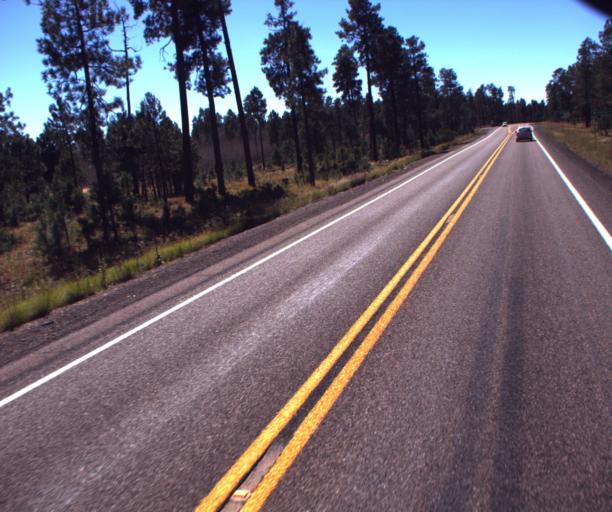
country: US
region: Arizona
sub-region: Navajo County
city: Heber-Overgaard
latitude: 34.3050
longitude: -110.8566
